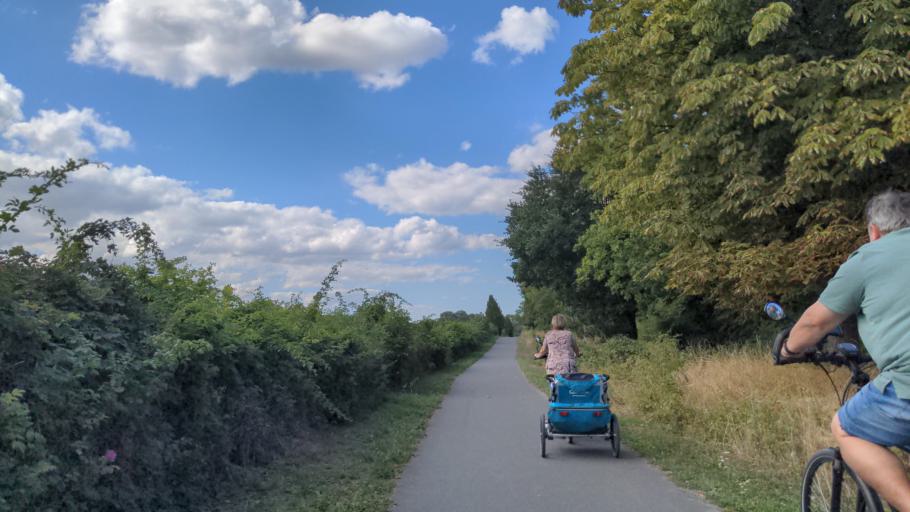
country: DE
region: Mecklenburg-Vorpommern
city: Wismar
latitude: 53.9155
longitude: 11.4152
